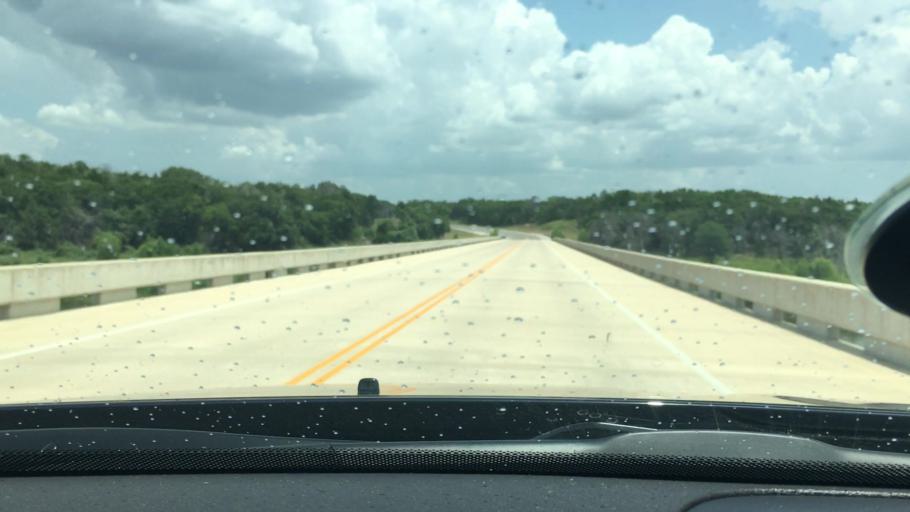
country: US
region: Oklahoma
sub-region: Love County
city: Marietta
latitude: 33.9728
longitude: -96.9952
